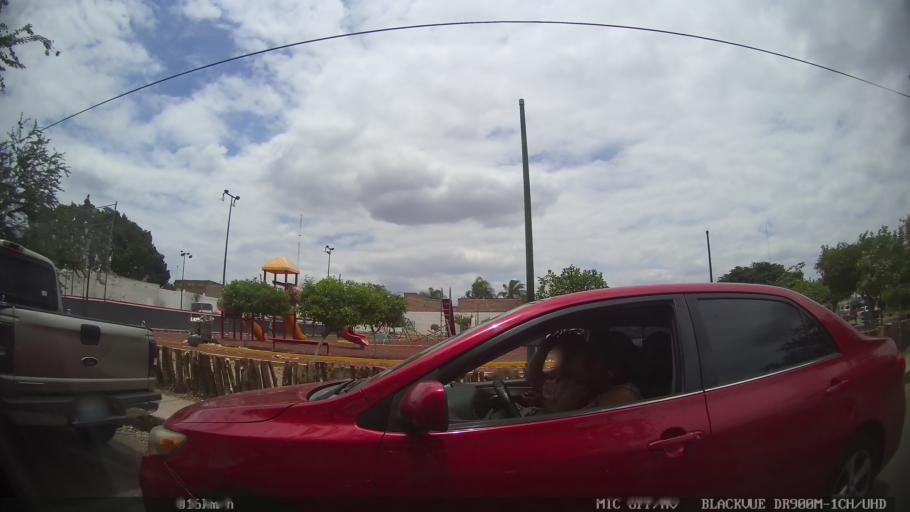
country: MX
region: Jalisco
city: Tlaquepaque
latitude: 20.6452
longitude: -103.2627
